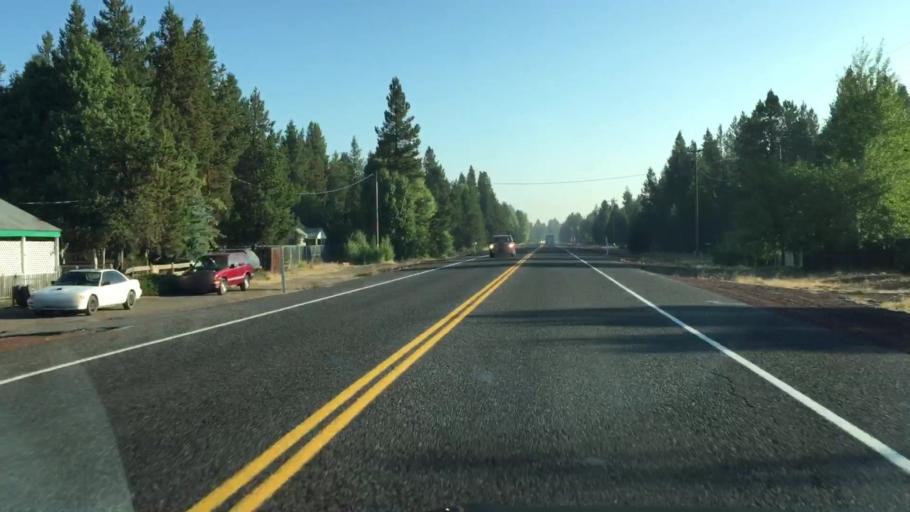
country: US
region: Oregon
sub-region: Deschutes County
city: La Pine
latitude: 43.4532
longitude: -121.7032
